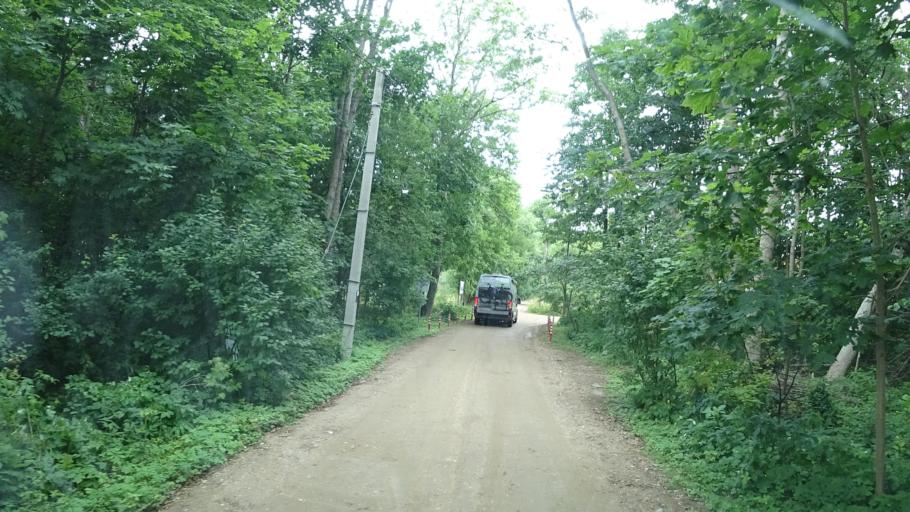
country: LT
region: Klaipedos apskritis
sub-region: Klaipeda
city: Klaipeda
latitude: 55.8027
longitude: 21.0714
